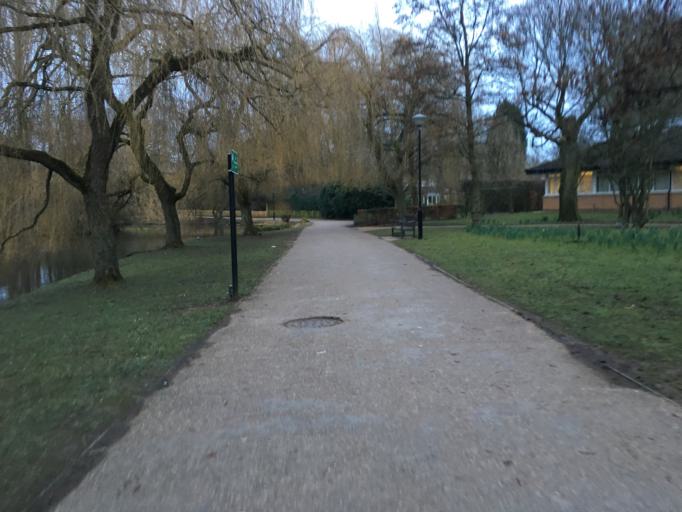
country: GB
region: England
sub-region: City of York
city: Heslington
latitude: 53.9464
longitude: -1.0527
